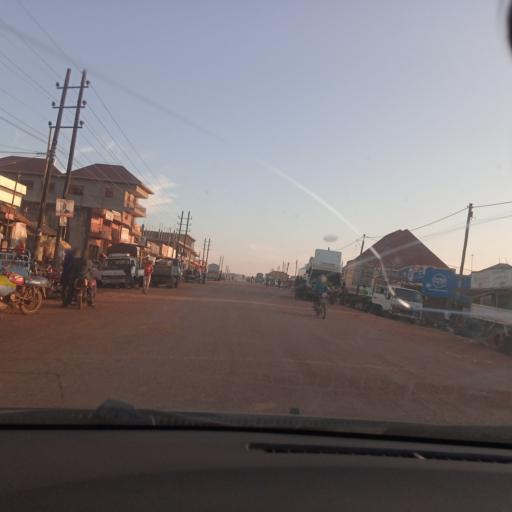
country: UG
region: Central Region
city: Masaka
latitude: -0.3206
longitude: 31.7574
